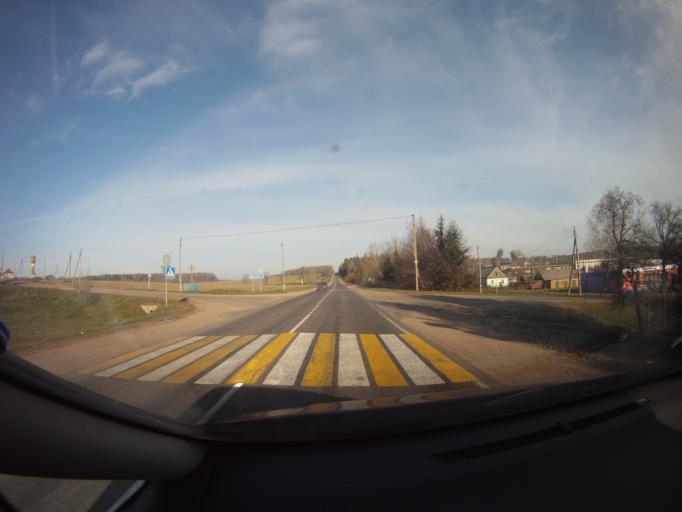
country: BY
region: Minsk
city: Il'ya
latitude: 54.4515
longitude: 27.2845
